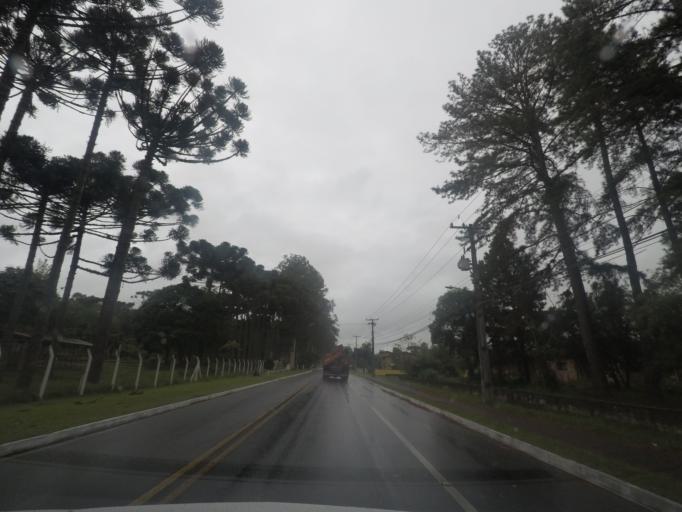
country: BR
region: Parana
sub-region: Quatro Barras
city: Quatro Barras
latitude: -25.3813
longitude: -49.1266
